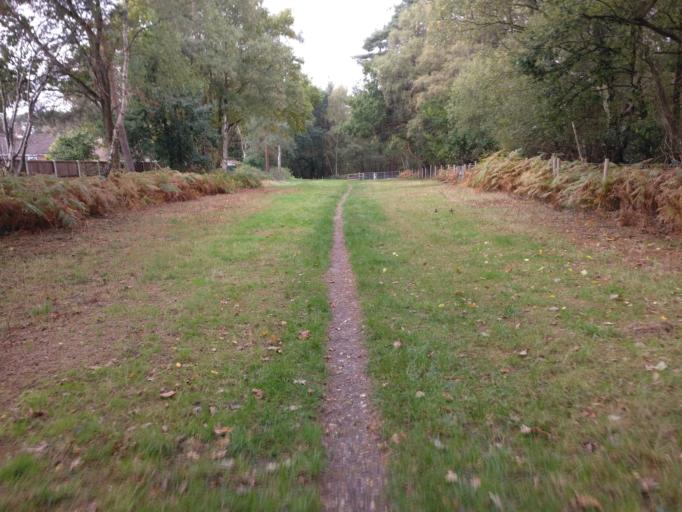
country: GB
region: England
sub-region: Surrey
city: Camberley
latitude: 51.3505
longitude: -0.7297
